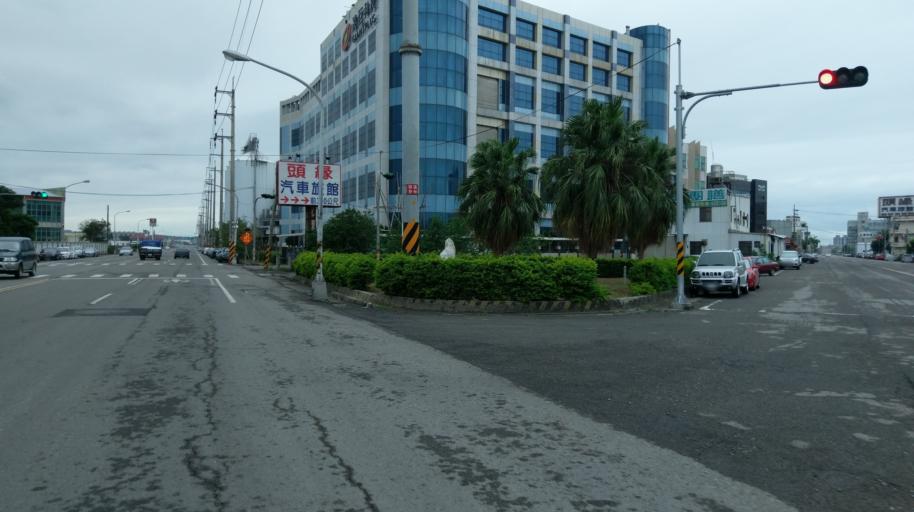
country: TW
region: Taiwan
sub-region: Miaoli
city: Miaoli
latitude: 24.6731
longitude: 120.8898
